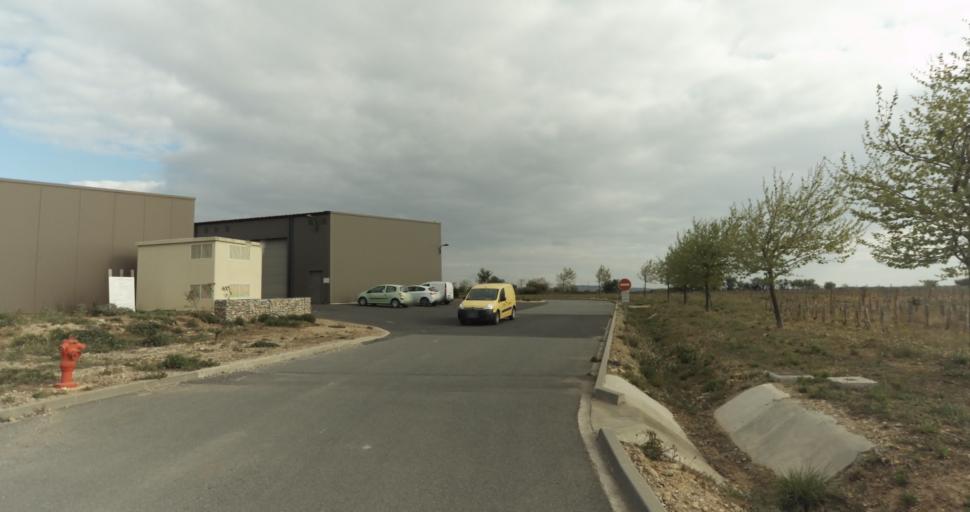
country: FR
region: Languedoc-Roussillon
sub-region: Departement de l'Aude
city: Leucate
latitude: 42.9330
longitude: 2.9960
